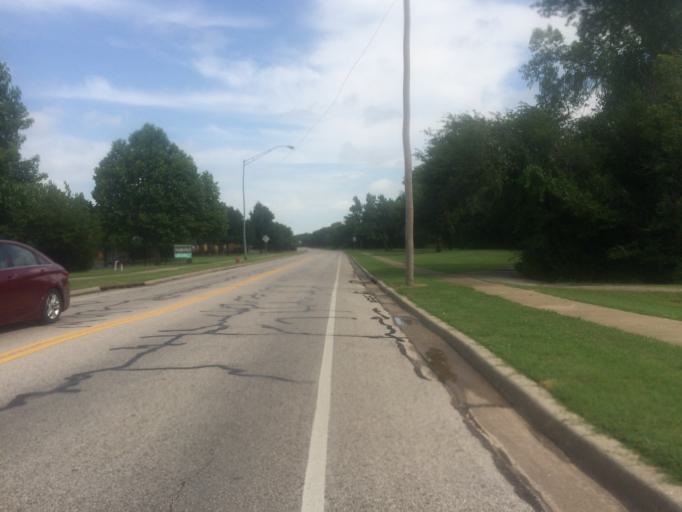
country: US
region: Oklahoma
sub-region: Cleveland County
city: Norman
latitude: 35.1878
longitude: -97.4236
